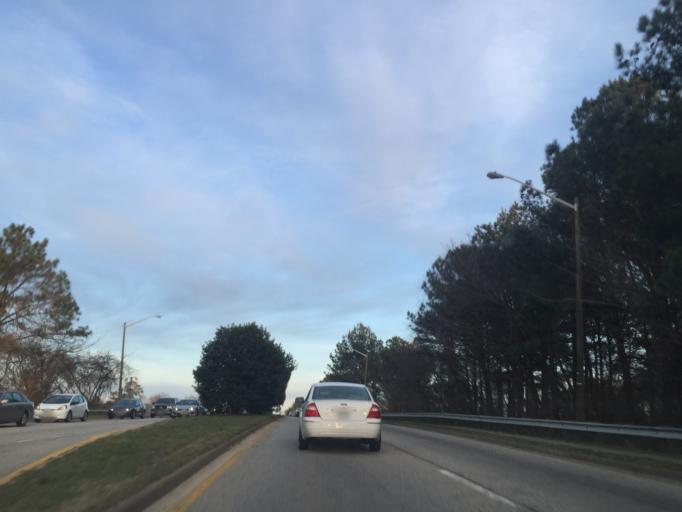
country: US
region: Virginia
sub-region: York County
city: Yorktown
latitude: 37.1060
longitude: -76.5049
